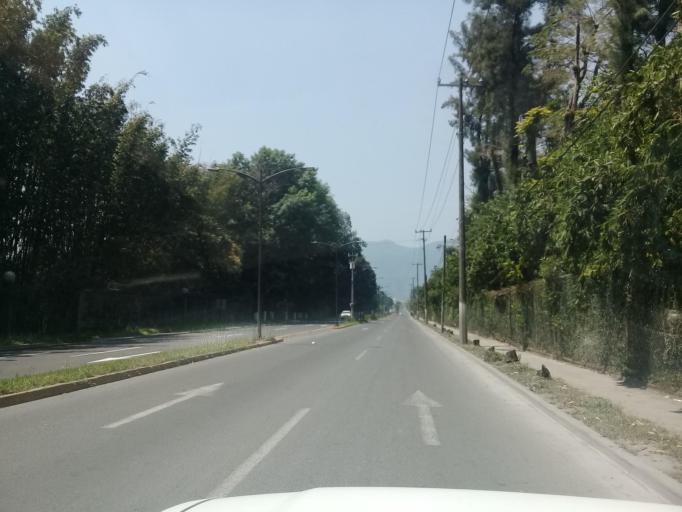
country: MX
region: Veracruz
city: Ixtac Zoquitlan
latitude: 18.8618
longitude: -97.0438
